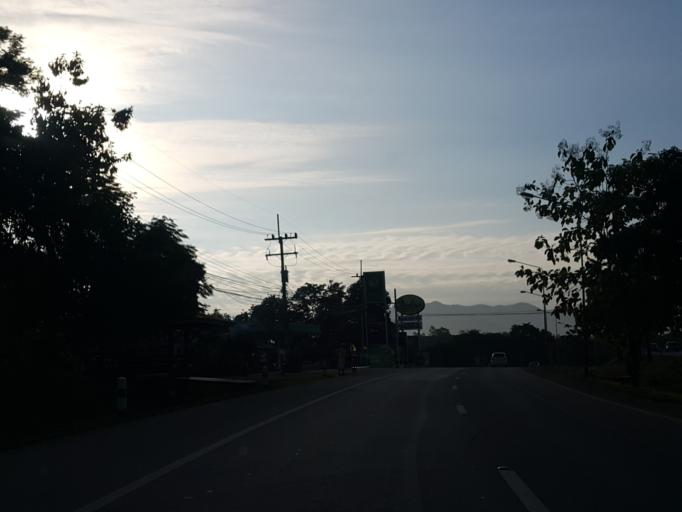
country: TH
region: Lampang
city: Lampang
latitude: 18.2824
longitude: 99.5196
